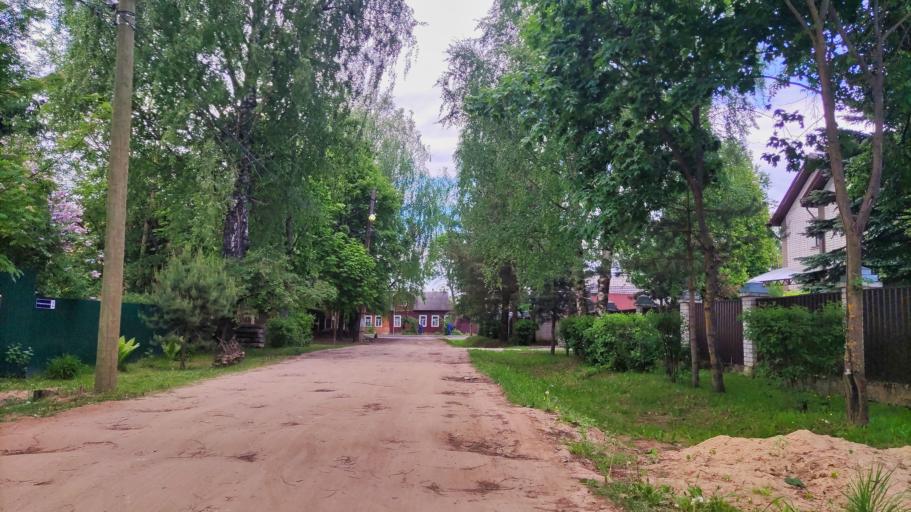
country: RU
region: Tverskaya
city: Rzhev
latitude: 56.2483
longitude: 34.3032
